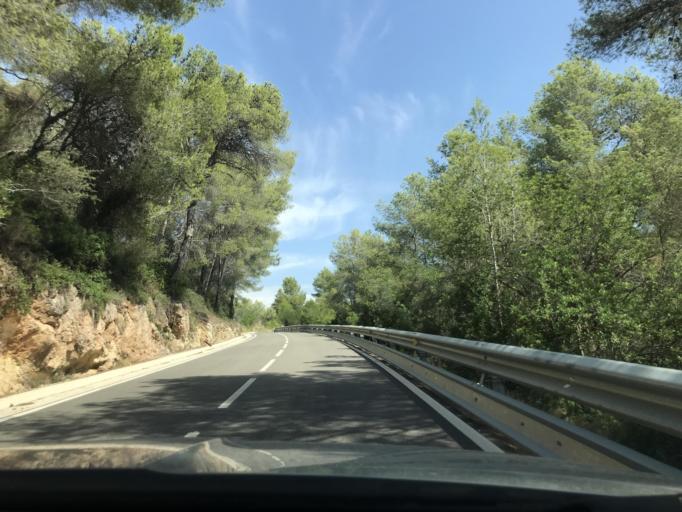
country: ES
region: Catalonia
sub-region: Provincia de Tarragona
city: Salomo
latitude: 41.1993
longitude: 1.3860
